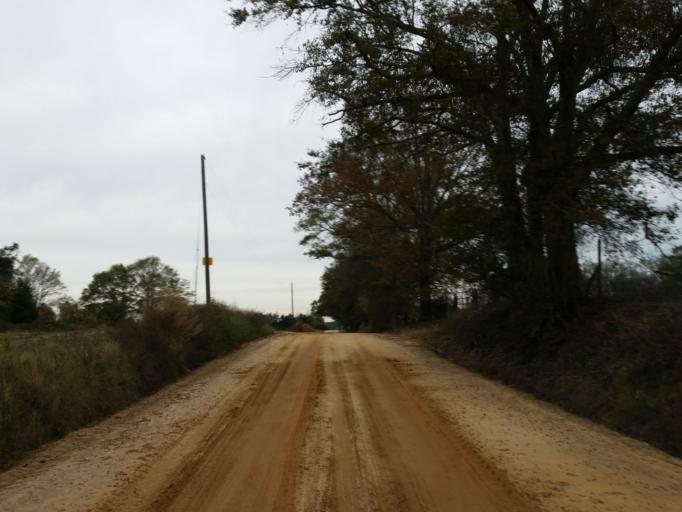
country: US
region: Georgia
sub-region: Crisp County
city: Cordele
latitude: 31.9157
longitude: -83.7284
